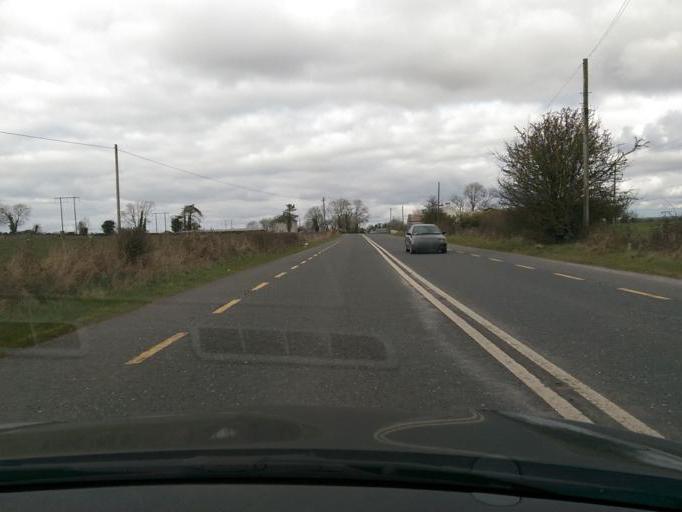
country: IE
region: Leinster
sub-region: An Iarmhi
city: Athlone
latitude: 53.3888
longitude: -7.9921
